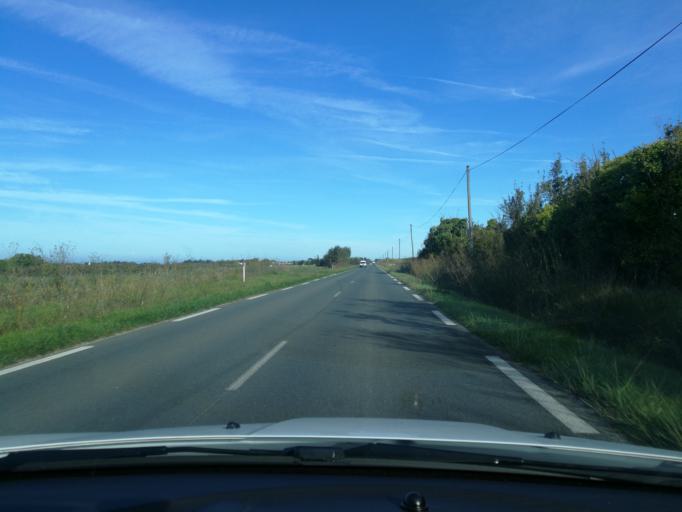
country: FR
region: Poitou-Charentes
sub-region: Departement de la Charente-Maritime
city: Saint-Denis-d'Oleron
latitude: 46.0068
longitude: -1.3687
